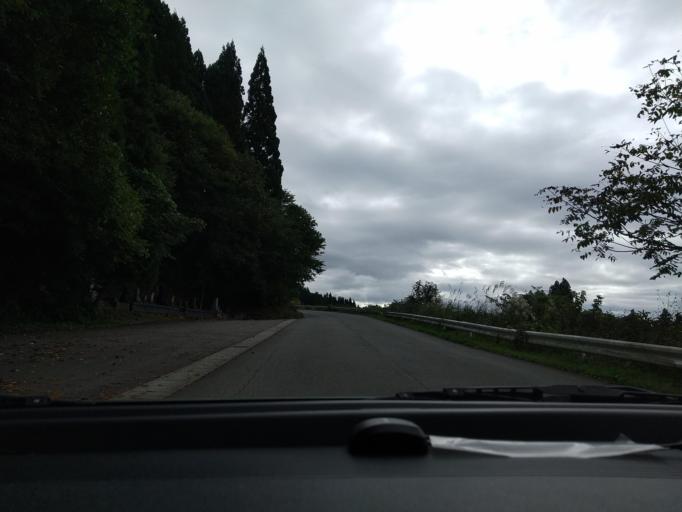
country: JP
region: Akita
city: Kakunodatemachi
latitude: 39.5873
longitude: 140.6188
